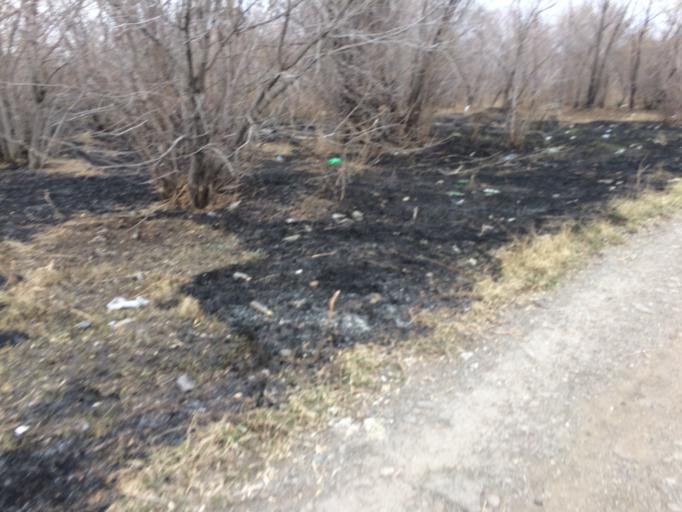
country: RU
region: Chelyabinsk
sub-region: Gorod Magnitogorsk
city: Magnitogorsk
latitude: 53.4398
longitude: 58.9769
